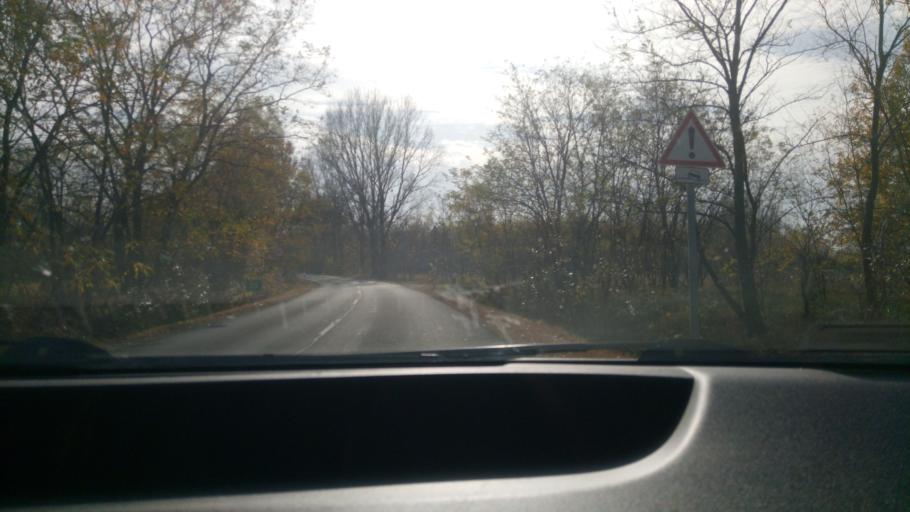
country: HU
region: Bacs-Kiskun
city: Jaszszentlaszlo
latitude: 46.5595
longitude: 19.7464
